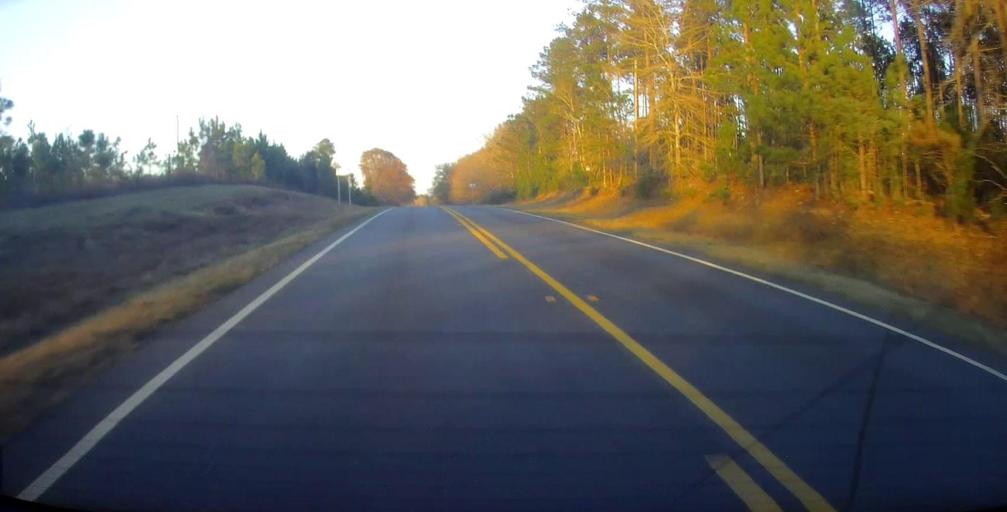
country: US
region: Georgia
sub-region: Dodge County
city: Chester
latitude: 32.3096
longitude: -83.0669
